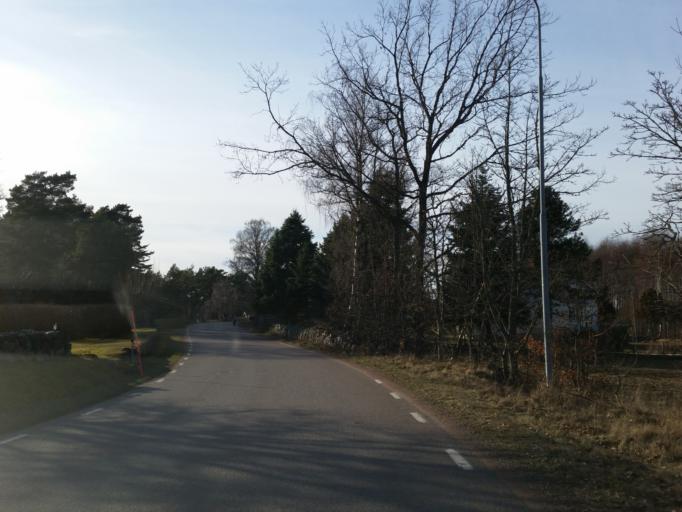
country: SE
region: Kalmar
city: Faerjestaden
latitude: 56.7826
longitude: 16.4454
